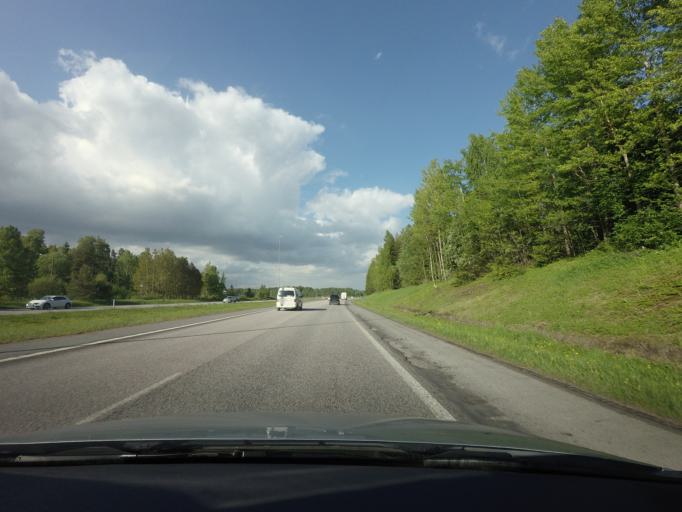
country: FI
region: Uusimaa
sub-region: Porvoo
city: Porvoo
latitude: 60.3551
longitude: 25.5256
